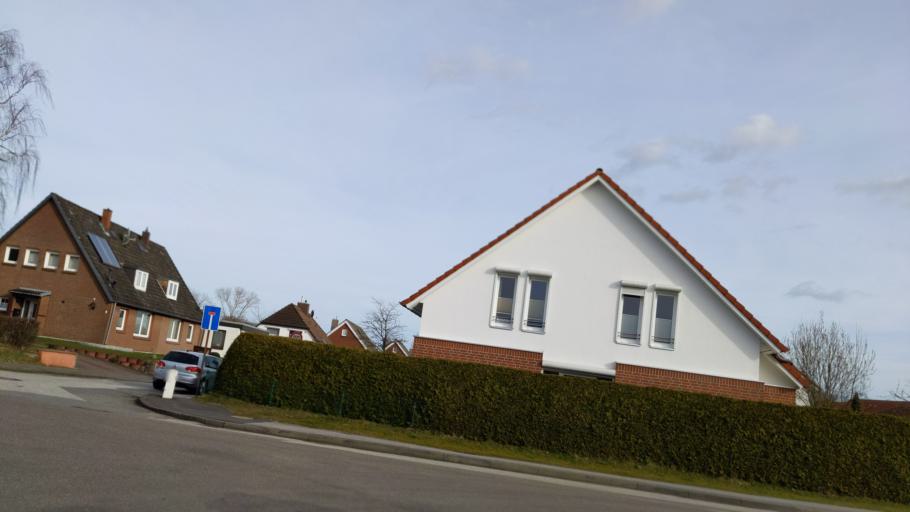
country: DE
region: Mecklenburg-Vorpommern
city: Selmsdorf
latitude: 53.9119
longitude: 10.8238
